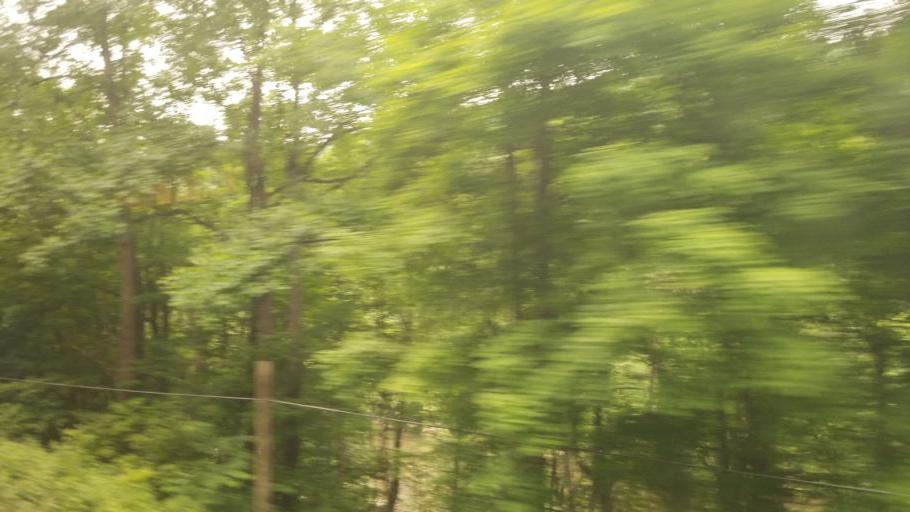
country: US
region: Pennsylvania
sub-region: Fayette County
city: South Connellsville
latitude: 39.9122
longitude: -79.4762
